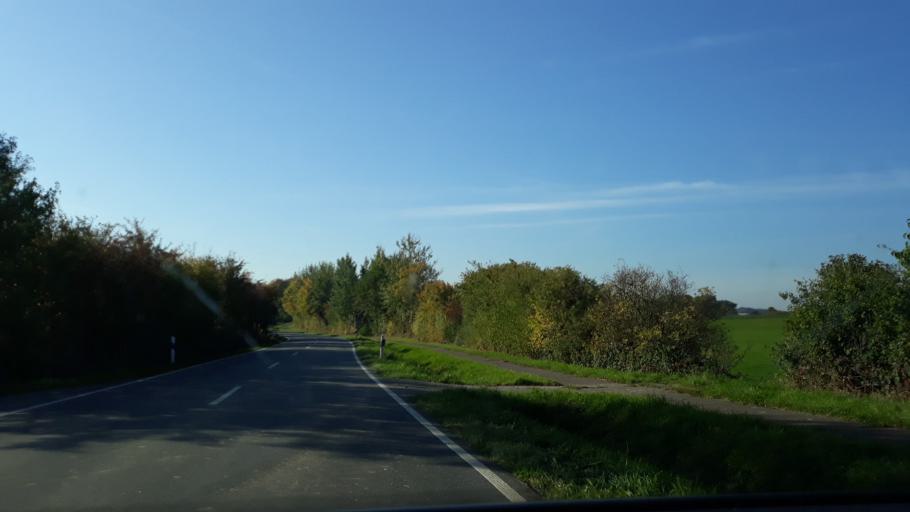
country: DE
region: Schleswig-Holstein
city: Ulsby
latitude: 54.6199
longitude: 9.5938
